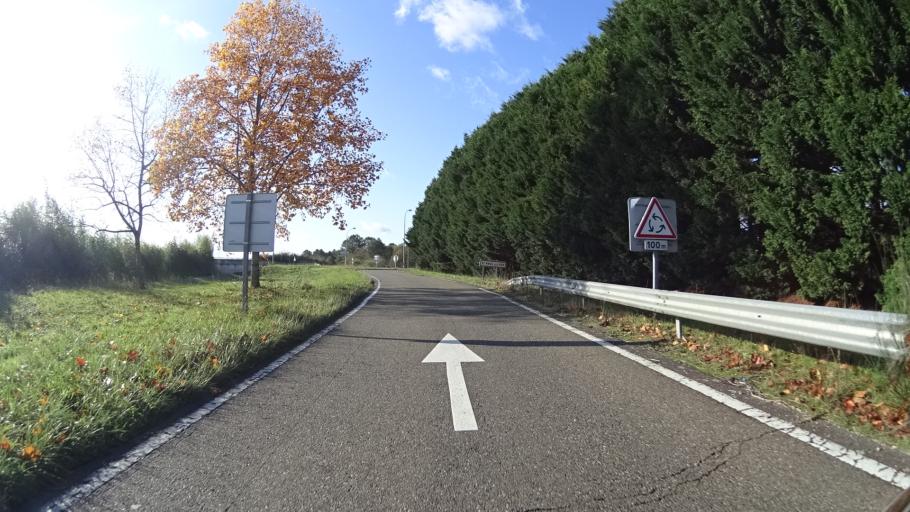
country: FR
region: Aquitaine
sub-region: Departement des Landes
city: Saint-Paul-les-Dax
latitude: 43.7450
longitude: -1.0542
